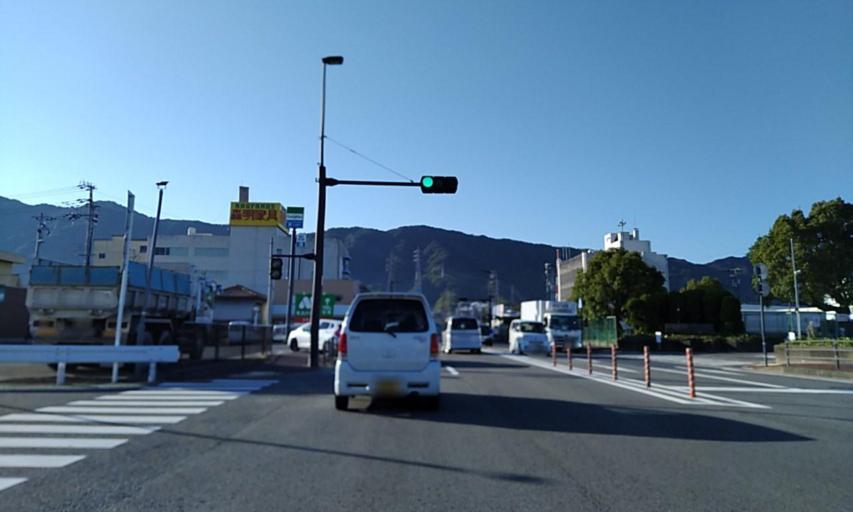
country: JP
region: Wakayama
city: Kainan
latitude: 34.1556
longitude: 135.2055
